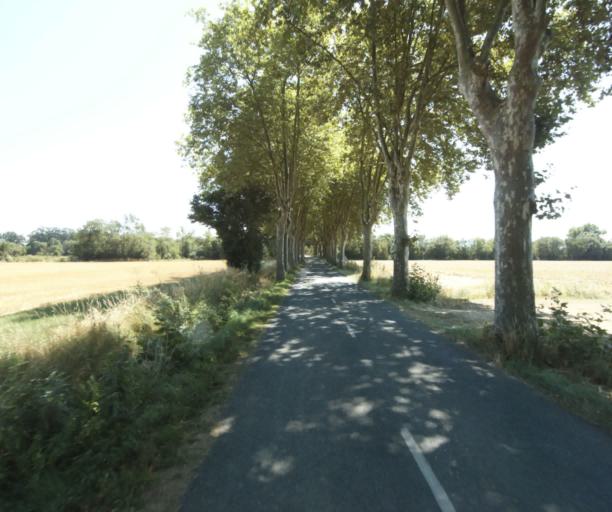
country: FR
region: Midi-Pyrenees
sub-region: Departement de la Haute-Garonne
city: Revel
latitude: 43.4979
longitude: 1.9614
